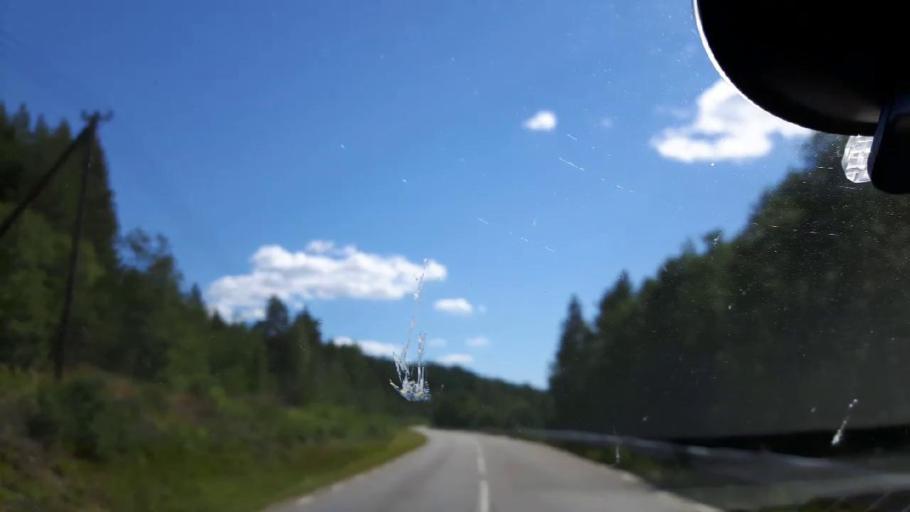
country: SE
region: Vaesternorrland
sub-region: Ange Kommun
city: Fransta
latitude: 62.7302
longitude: 16.3292
